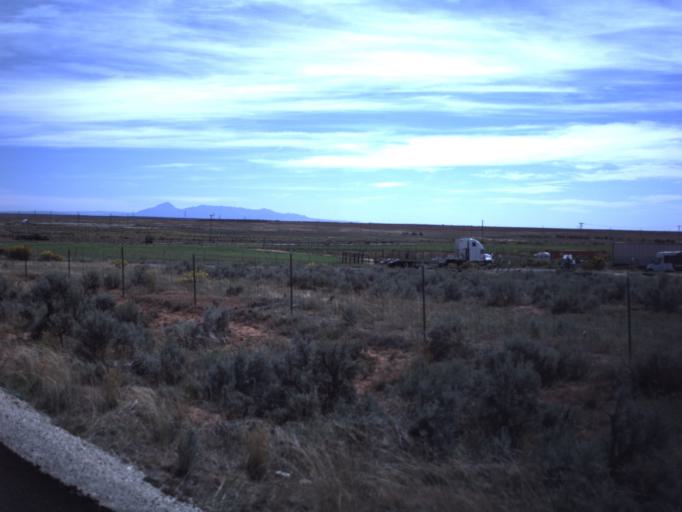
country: US
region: Utah
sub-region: San Juan County
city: Blanding
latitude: 37.5736
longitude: -109.4927
